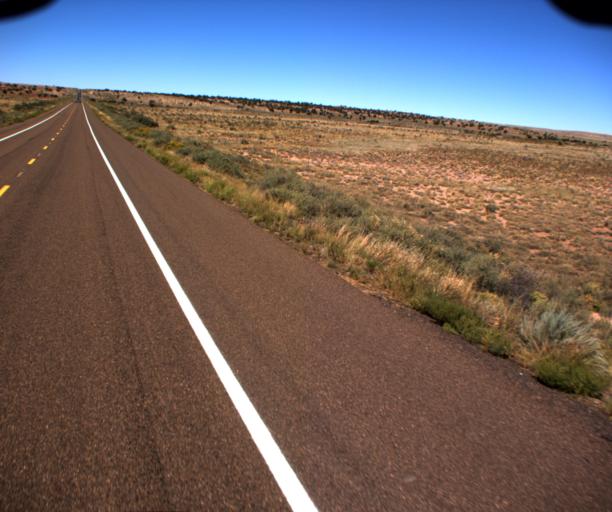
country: US
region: Arizona
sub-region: Navajo County
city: Snowflake
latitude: 34.6637
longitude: -109.7181
